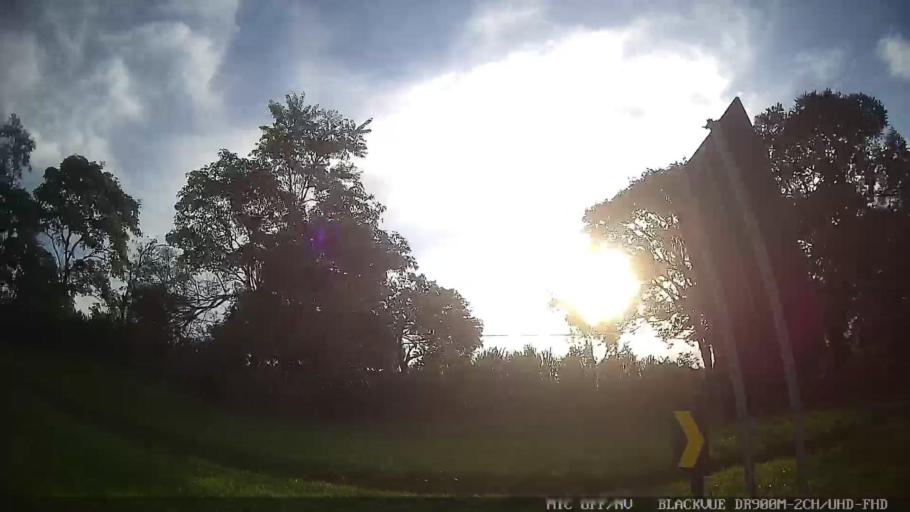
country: BR
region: Sao Paulo
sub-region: Tiete
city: Tiete
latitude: -23.1421
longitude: -47.6767
